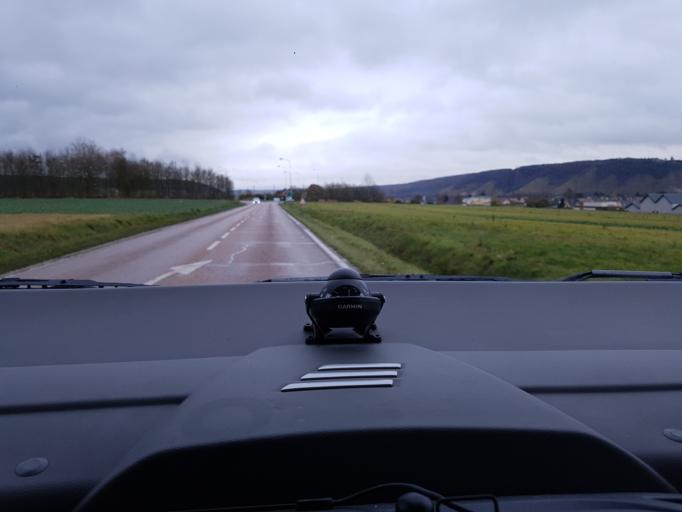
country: FR
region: Haute-Normandie
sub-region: Departement de l'Eure
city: Le Manoir
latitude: 49.3260
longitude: 1.2152
